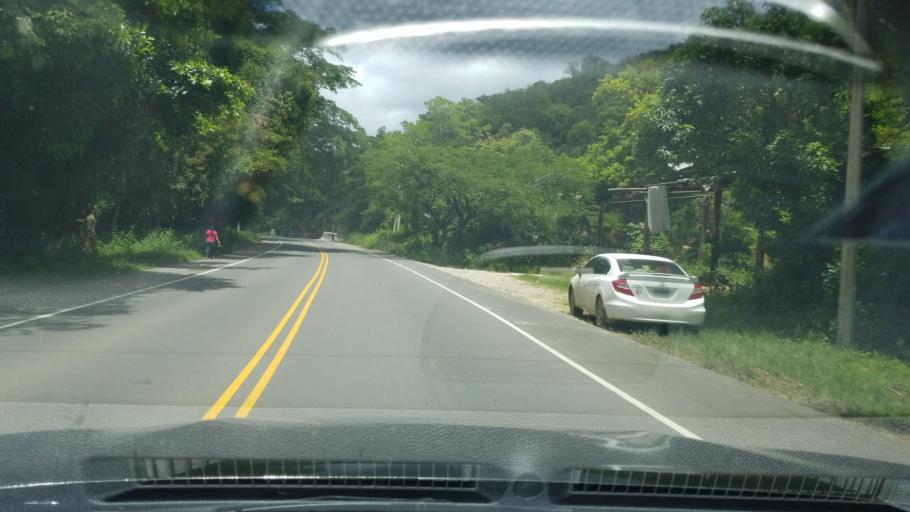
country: HN
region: Francisco Morazan
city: Talanga
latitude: 14.3790
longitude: -87.1369
